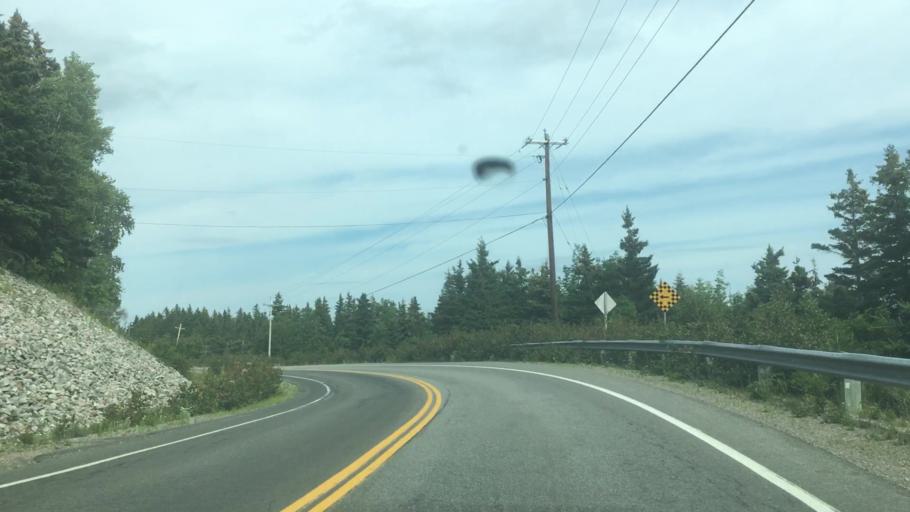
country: CA
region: Nova Scotia
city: Sydney Mines
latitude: 46.5347
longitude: -60.4152
